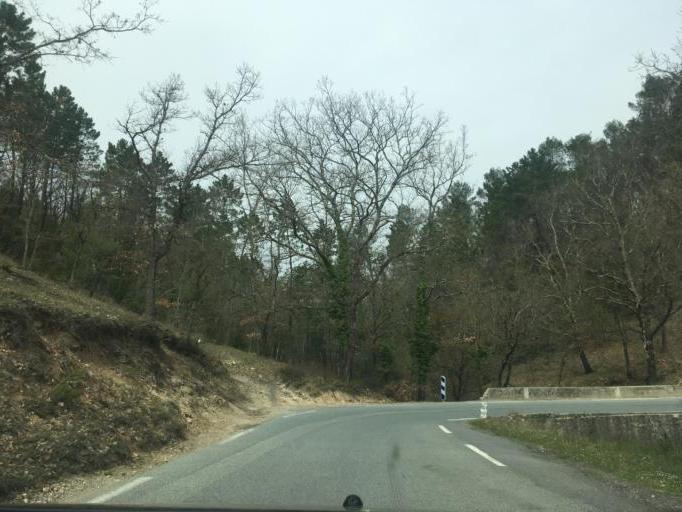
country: FR
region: Provence-Alpes-Cote d'Azur
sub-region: Departement du Var
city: Saint-Paul-en-Foret
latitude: 43.5872
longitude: 6.7295
